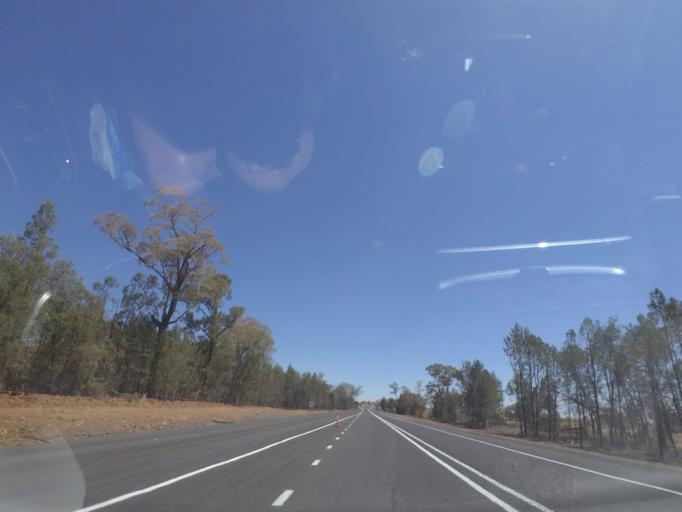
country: AU
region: New South Wales
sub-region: Gilgandra
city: Gilgandra
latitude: -31.6657
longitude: 148.7185
